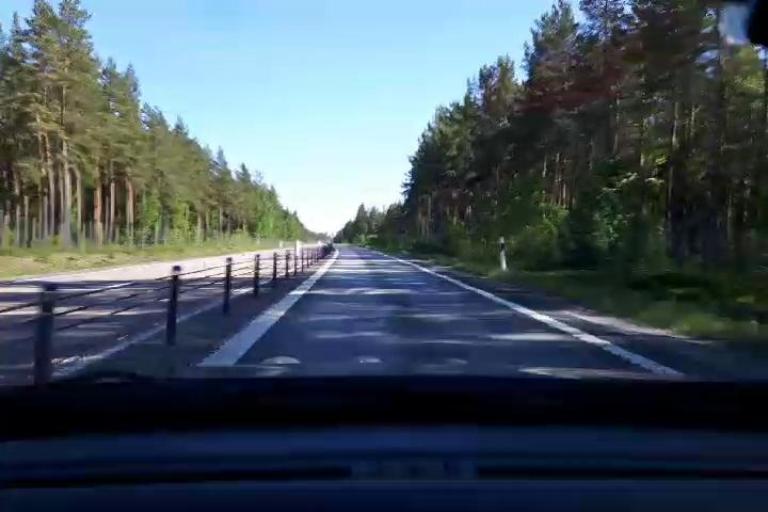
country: SE
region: Gaevleborg
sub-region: Gavle Kommun
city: Norrsundet
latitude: 60.9954
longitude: 16.9969
